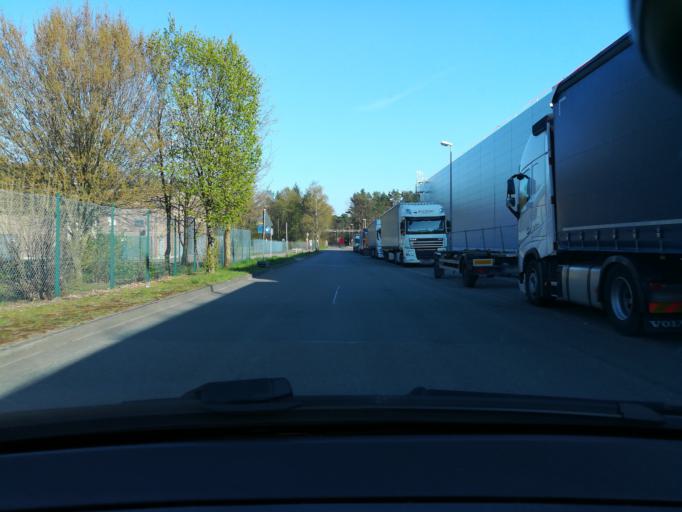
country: DE
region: North Rhine-Westphalia
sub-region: Regierungsbezirk Detmold
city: Verl
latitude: 51.9440
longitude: 8.5661
